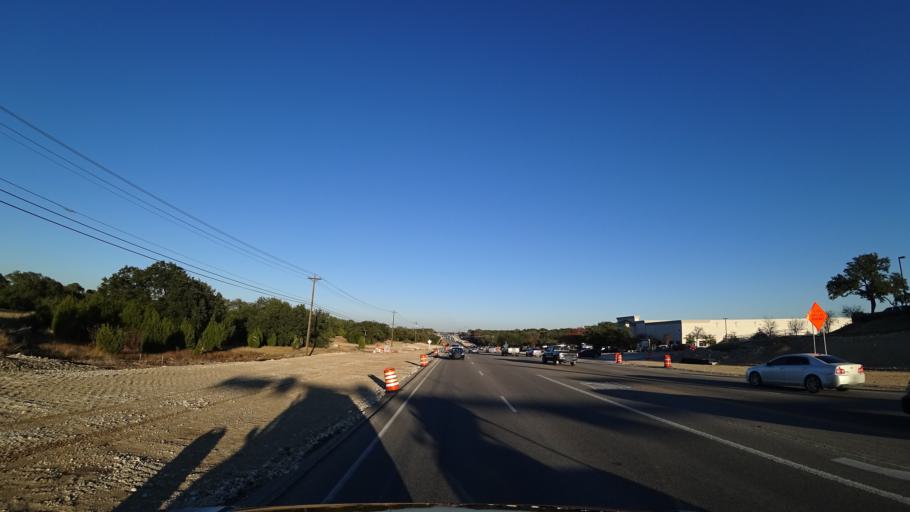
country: US
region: Texas
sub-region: Williamson County
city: Cedar Park
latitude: 30.5297
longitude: -97.8002
